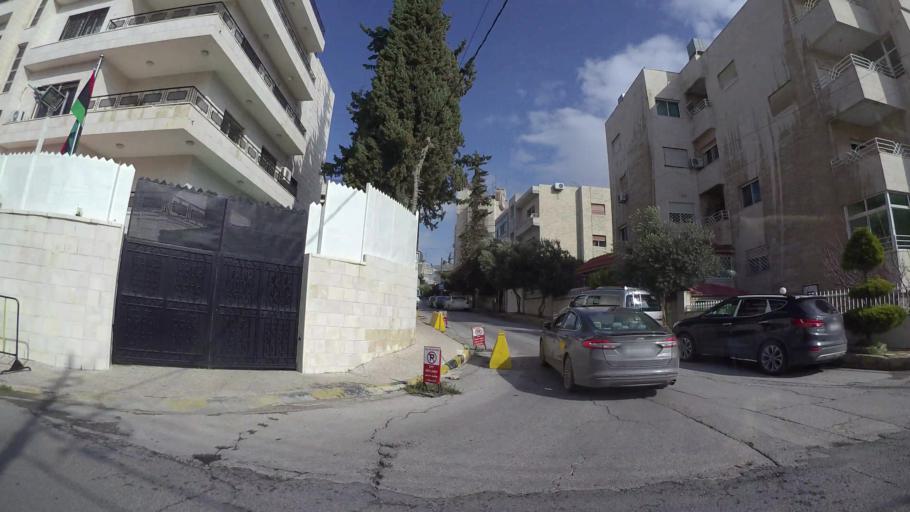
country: JO
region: Amman
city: Amman
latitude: 31.9657
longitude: 35.8890
